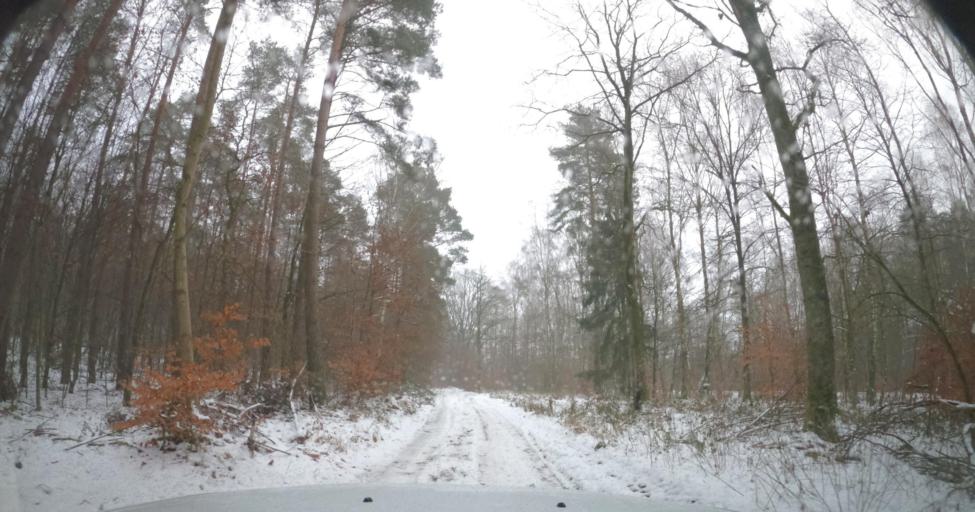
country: PL
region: West Pomeranian Voivodeship
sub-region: Powiat kamienski
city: Golczewo
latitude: 53.8692
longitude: 15.0456
